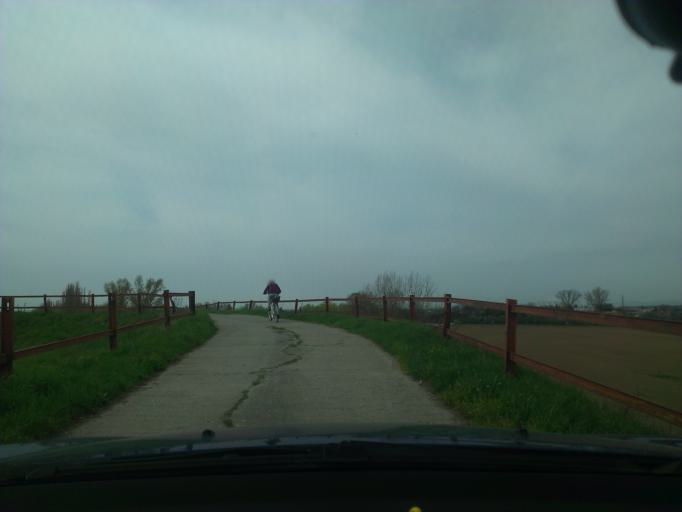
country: SK
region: Trnavsky
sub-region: Okres Trnava
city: Piestany
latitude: 48.5172
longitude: 17.8143
